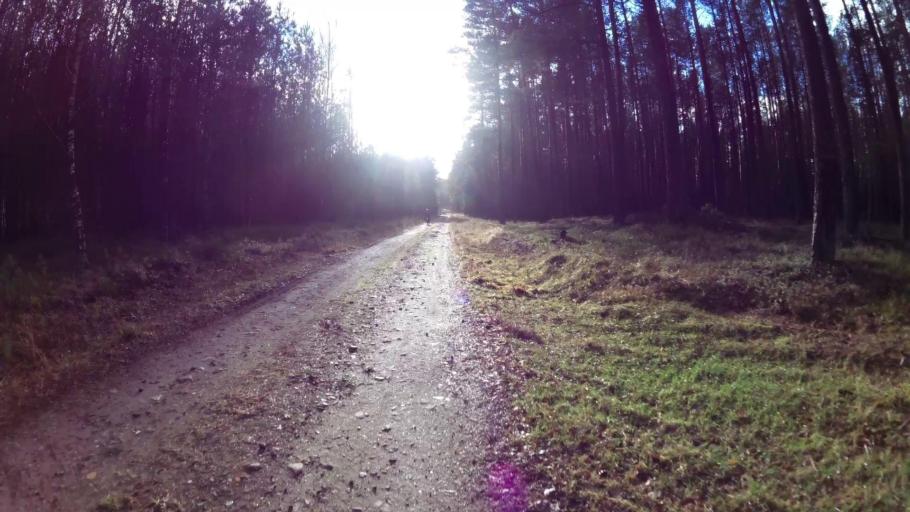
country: PL
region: West Pomeranian Voivodeship
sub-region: Powiat koszalinski
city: Sianow
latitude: 54.0871
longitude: 16.2926
